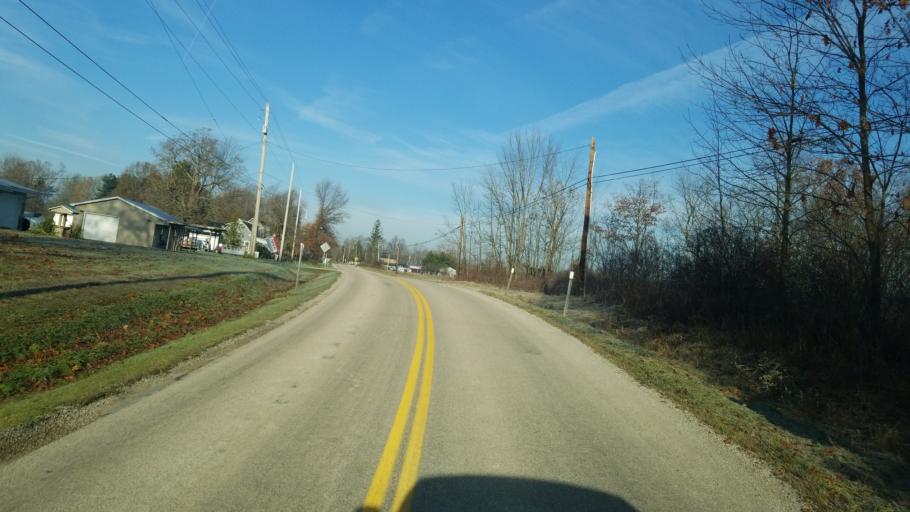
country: US
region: Ohio
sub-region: Ashtabula County
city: Andover
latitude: 41.6738
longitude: -80.6626
